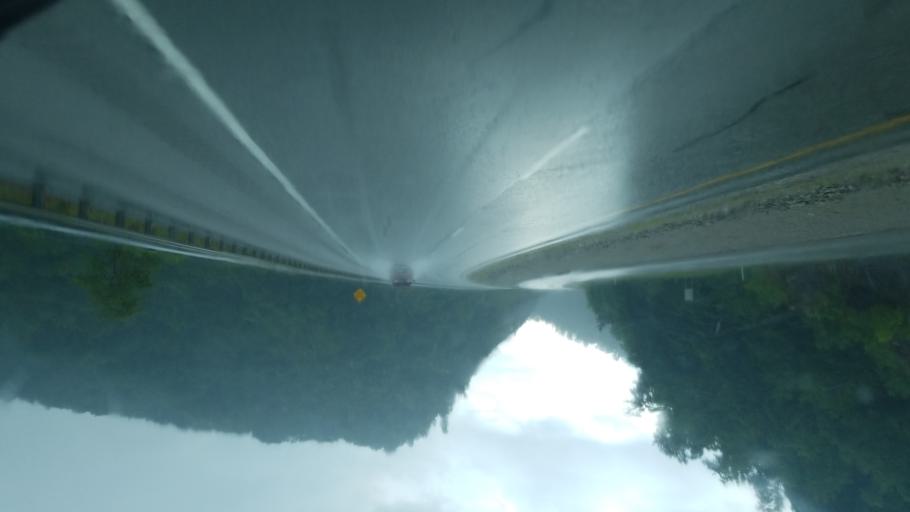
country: US
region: Kentucky
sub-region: Pike County
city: Pikeville
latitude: 37.5530
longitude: -82.4311
